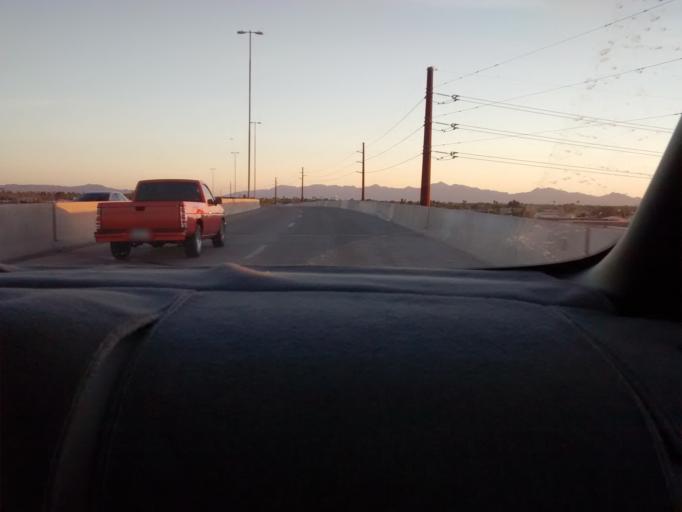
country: US
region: Arizona
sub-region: Maricopa County
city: Glendale
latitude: 33.5531
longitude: -112.2036
